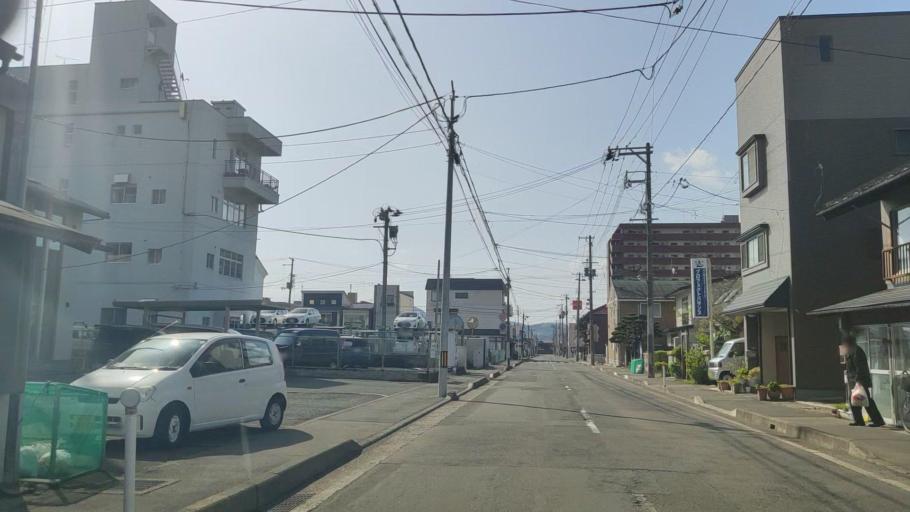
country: JP
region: Iwate
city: Morioka-shi
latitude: 39.6973
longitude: 141.1527
